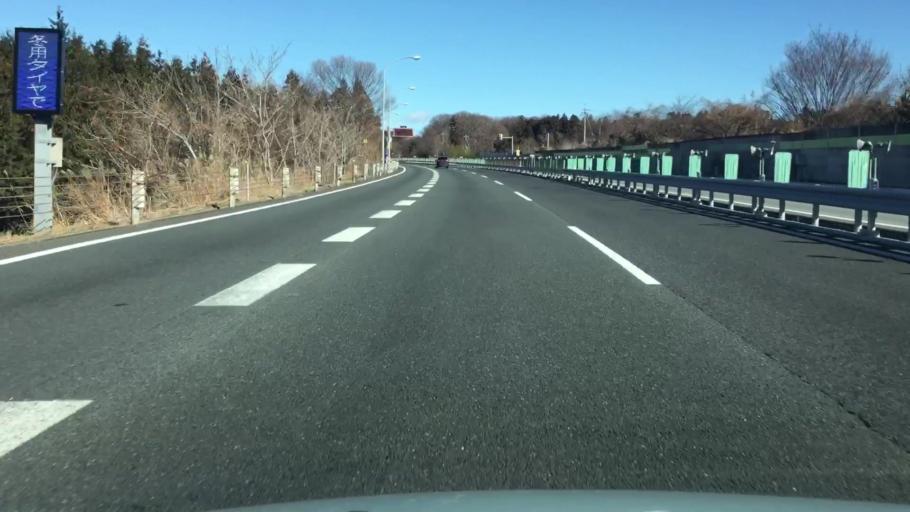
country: JP
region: Gunma
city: Shibukawa
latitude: 36.5316
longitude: 139.0457
